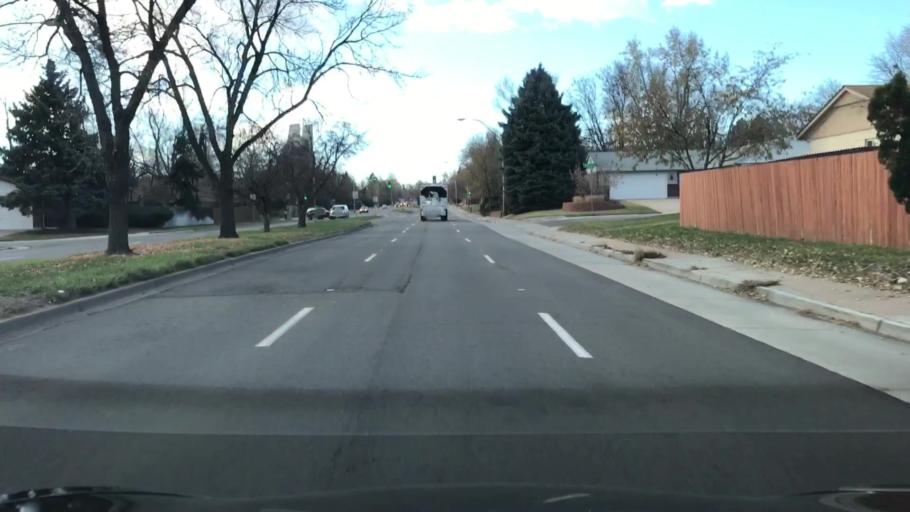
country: US
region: Colorado
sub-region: Arapahoe County
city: Glendale
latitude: 39.6640
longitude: -104.9131
